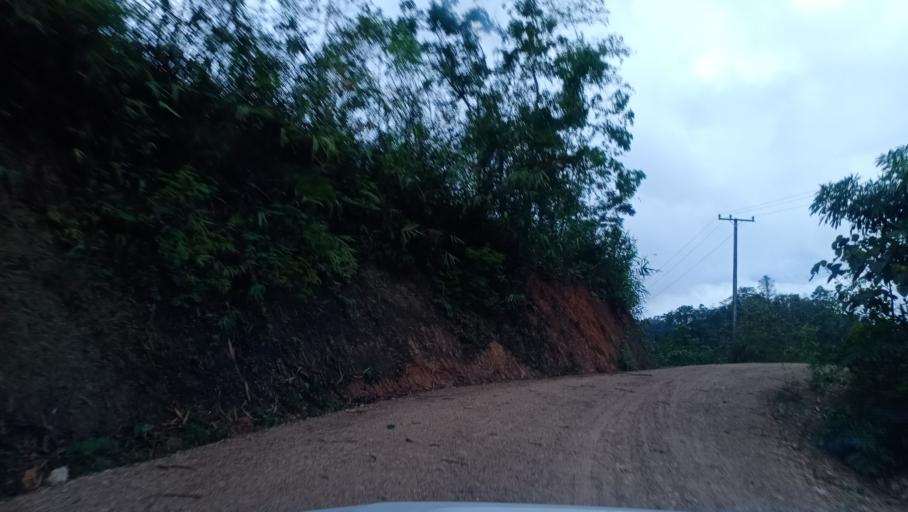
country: LA
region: Phongsali
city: Khoa
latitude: 21.2805
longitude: 102.7023
